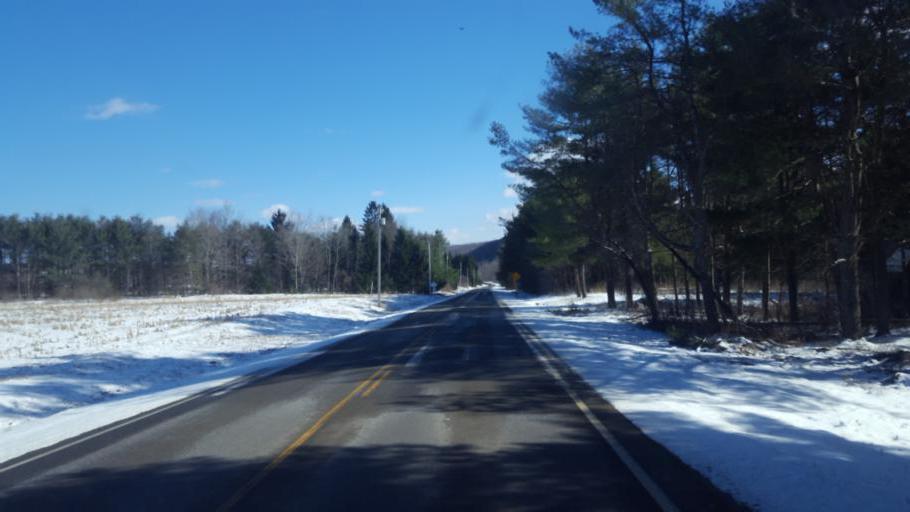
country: US
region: New York
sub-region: Allegany County
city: Belmont
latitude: 42.1790
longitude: -78.0737
